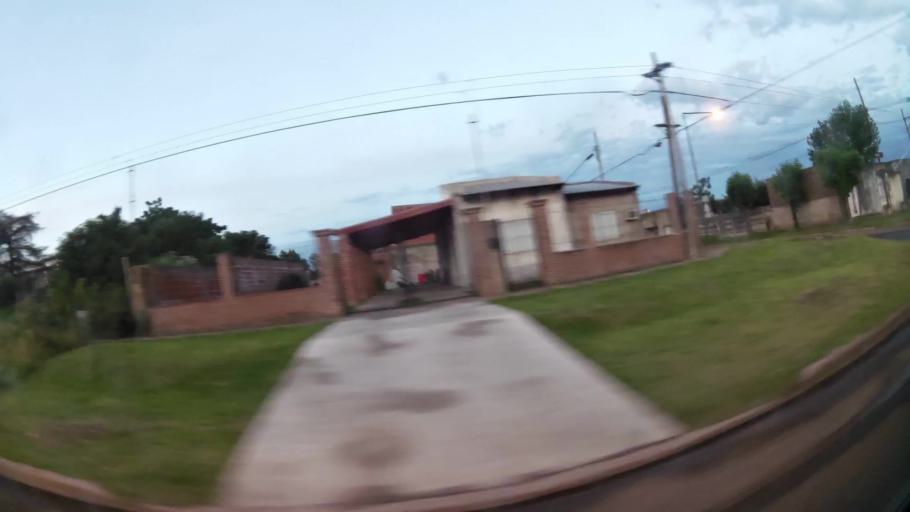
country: AR
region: Buenos Aires
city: San Nicolas de los Arroyos
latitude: -33.3534
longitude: -60.2121
